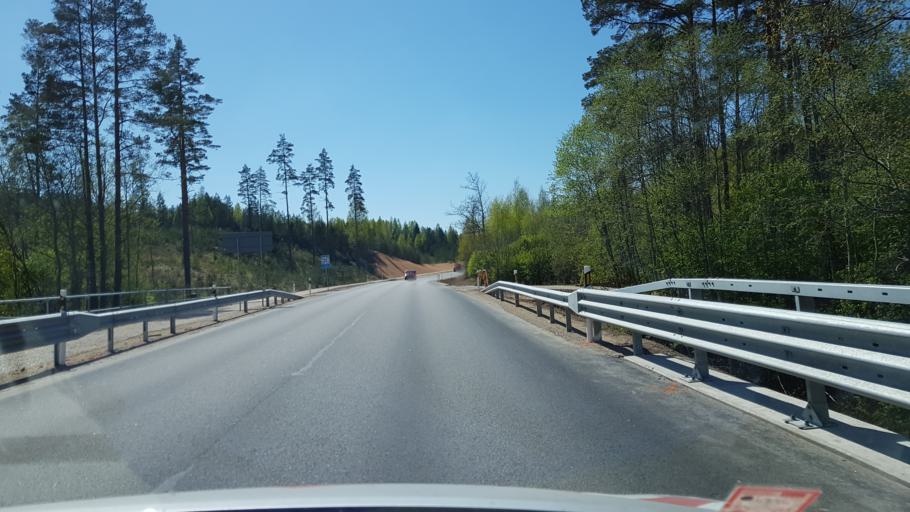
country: EE
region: Vorumaa
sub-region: Voru linn
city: Voru
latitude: 57.8782
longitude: 26.8255
